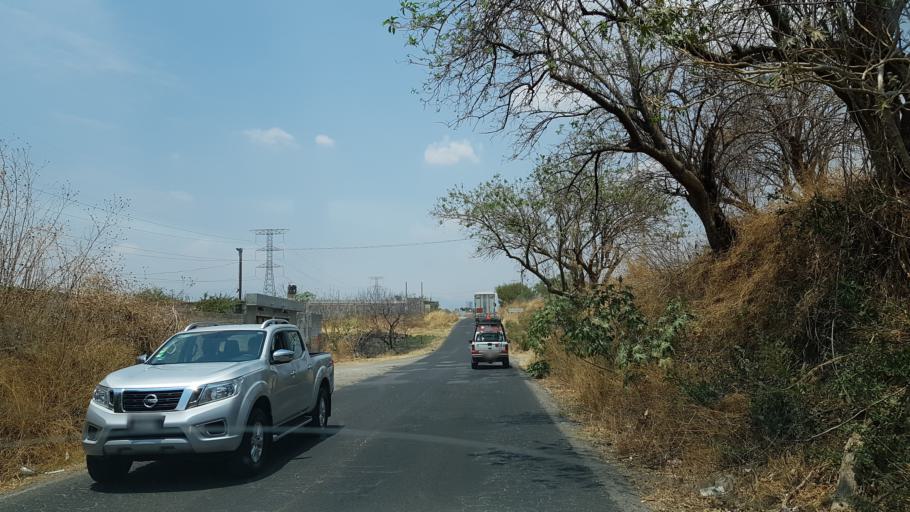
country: MX
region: Morelos
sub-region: Yecapixtla
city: Yecapixtla
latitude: 18.8854
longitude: -98.8847
